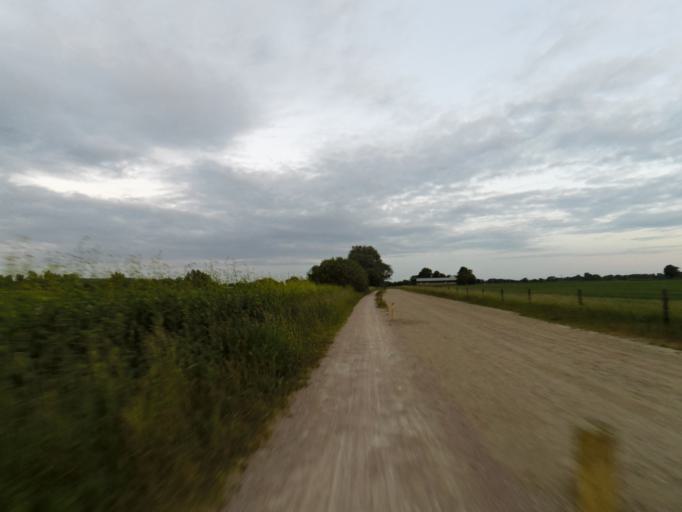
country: NL
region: Gelderland
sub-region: Gemeente Zevenaar
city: Zevenaar
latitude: 51.8789
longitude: 6.1338
